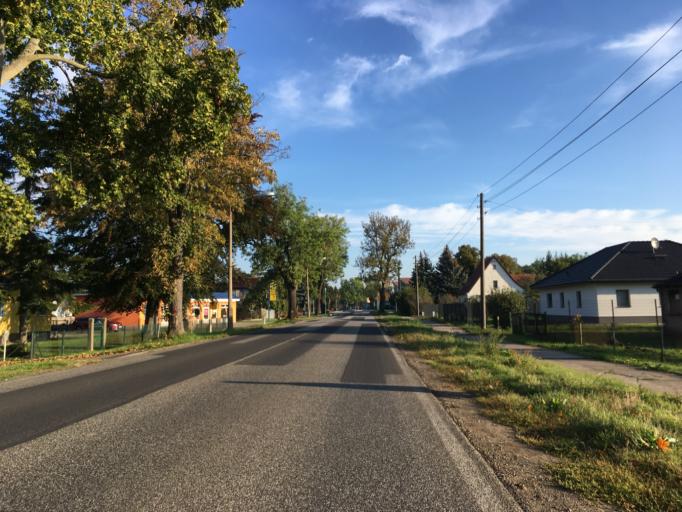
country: DE
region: Brandenburg
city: Lebus
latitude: 52.4240
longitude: 14.5317
